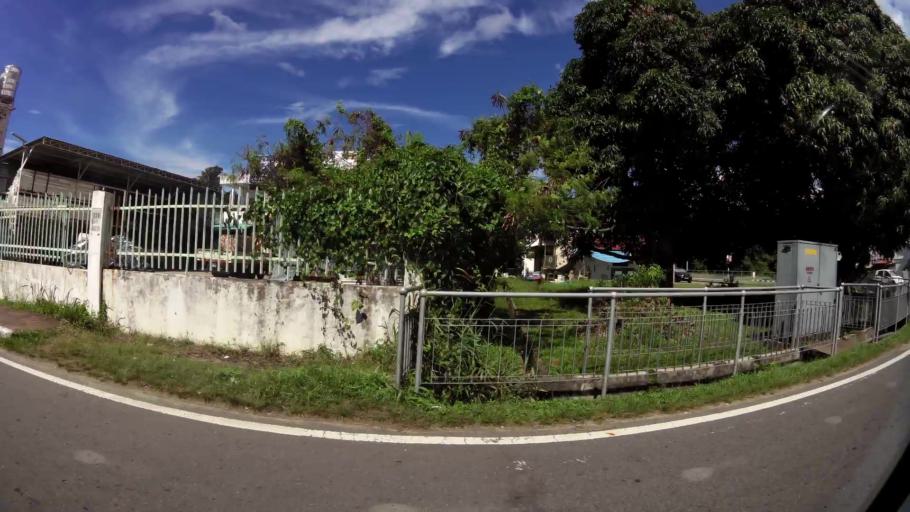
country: BN
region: Brunei and Muara
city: Bandar Seri Begawan
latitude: 4.9648
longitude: 114.9466
